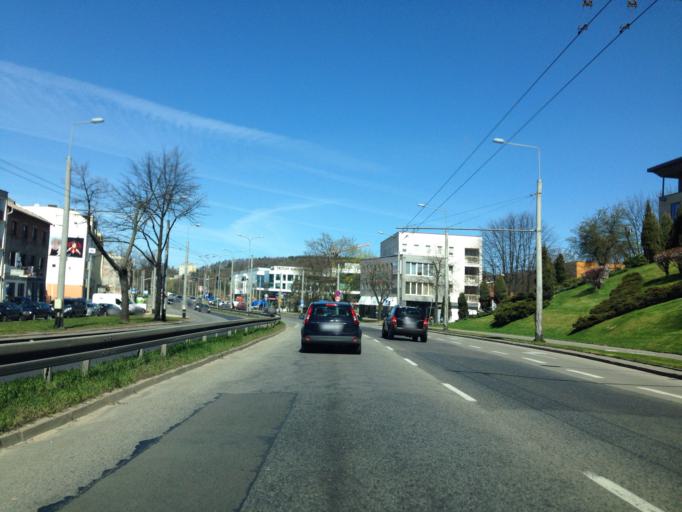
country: PL
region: Pomeranian Voivodeship
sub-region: Sopot
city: Sopot
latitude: 54.4778
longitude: 18.5531
